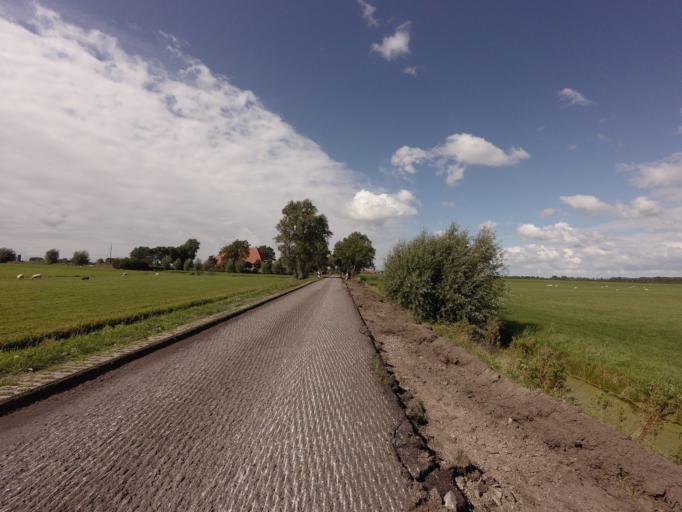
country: NL
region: Friesland
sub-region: Sudwest Fryslan
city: Bolsward
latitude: 53.0344
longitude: 5.5657
